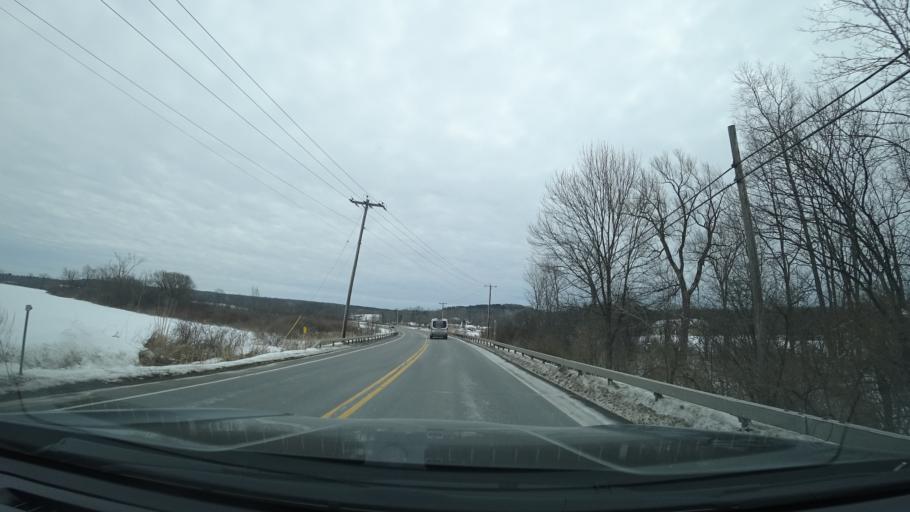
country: US
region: New York
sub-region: Washington County
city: Fort Edward
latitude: 43.2616
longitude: -73.5266
